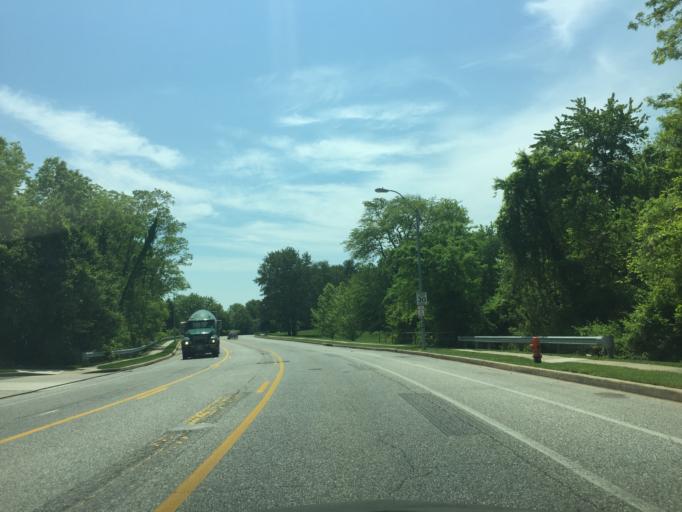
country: US
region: Maryland
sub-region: Baltimore County
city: Perry Hall
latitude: 39.4022
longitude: -76.4862
